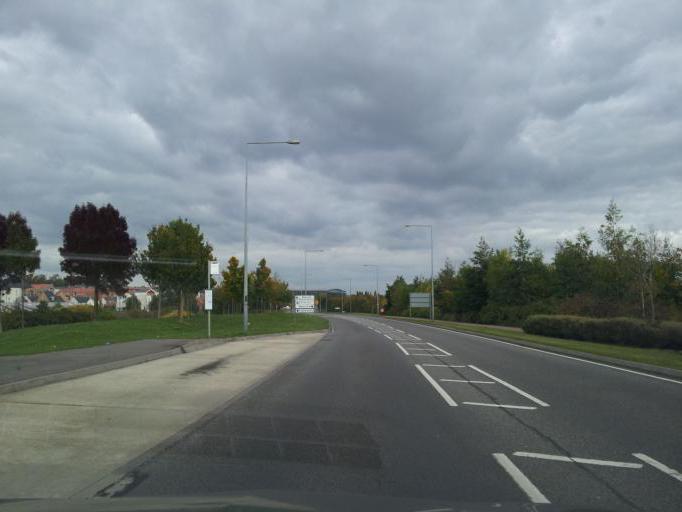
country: GB
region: England
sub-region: Milton Keynes
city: Shenley Church End
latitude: 52.0050
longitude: -0.8039
